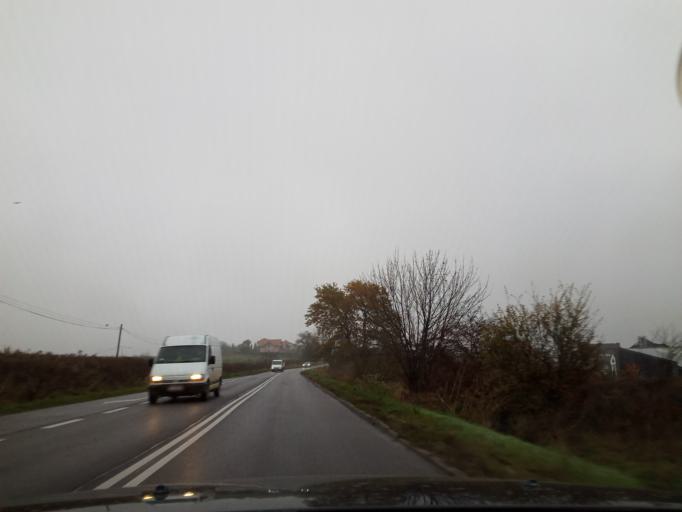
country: PL
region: Lesser Poland Voivodeship
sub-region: Powiat wielicki
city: Kokotow
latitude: 50.1064
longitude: 20.0752
